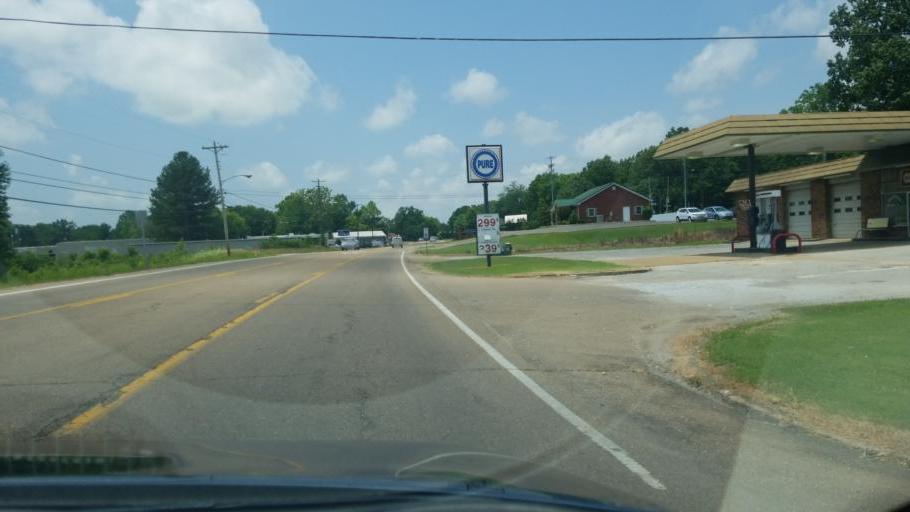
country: US
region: Tennessee
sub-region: Carroll County
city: Huntingdon
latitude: 36.0040
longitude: -88.4147
